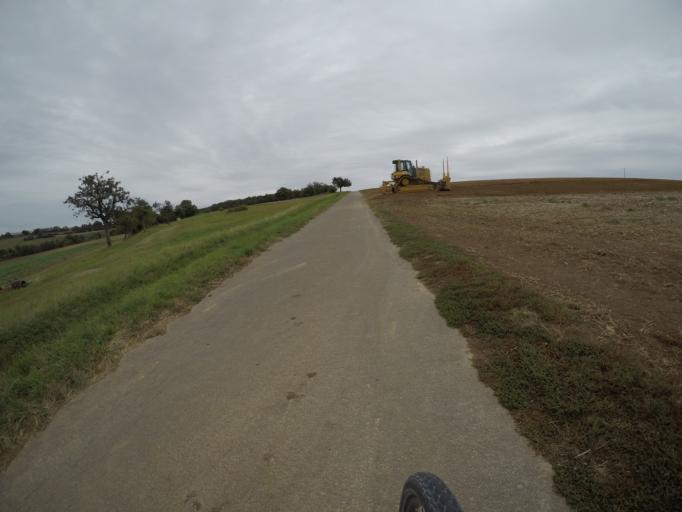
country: DE
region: Baden-Wuerttemberg
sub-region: Regierungsbezirk Stuttgart
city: Eberdingen
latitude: 48.8897
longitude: 8.9763
